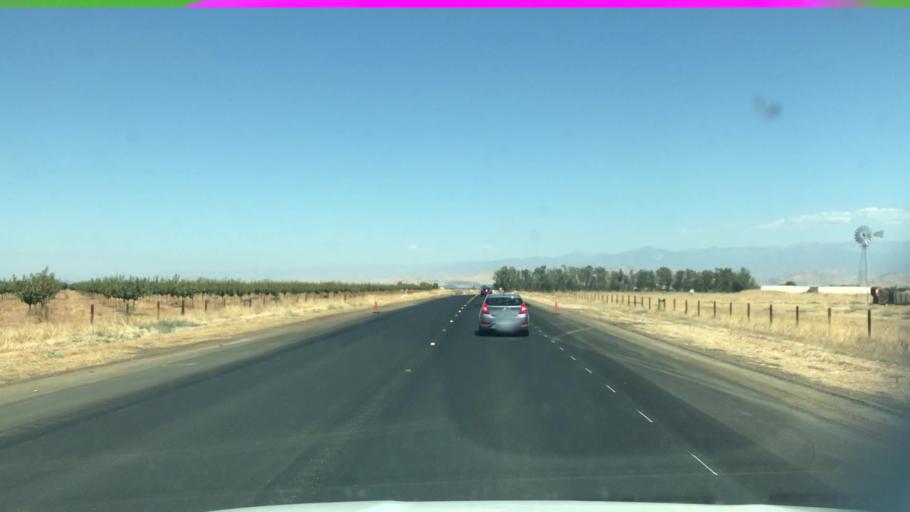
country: US
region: California
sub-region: Tulare County
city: Terra Bella
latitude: 35.9861
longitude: -119.0512
